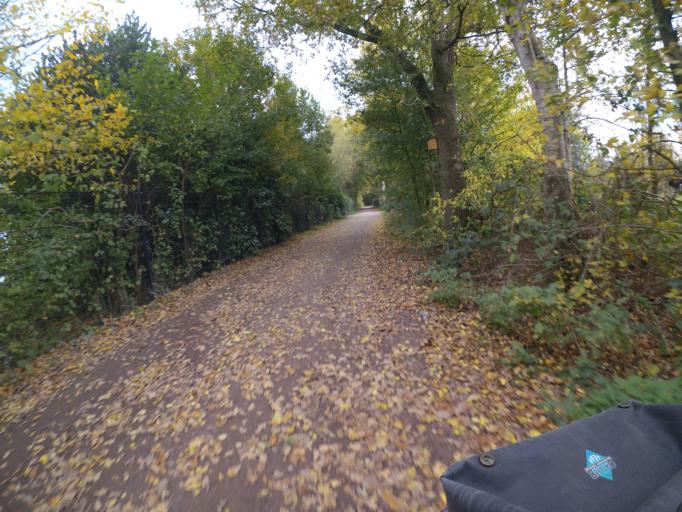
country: NL
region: North Brabant
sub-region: Gemeente Haaren
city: Haaren
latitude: 51.6180
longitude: 5.2566
